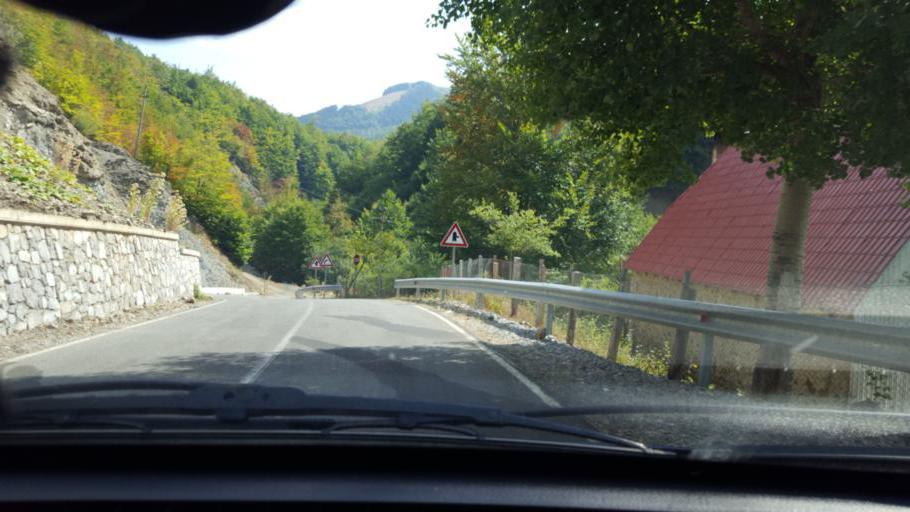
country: AL
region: Kukes
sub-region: Rrethi i Tropojes
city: Valbone
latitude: 42.5375
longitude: 19.6988
